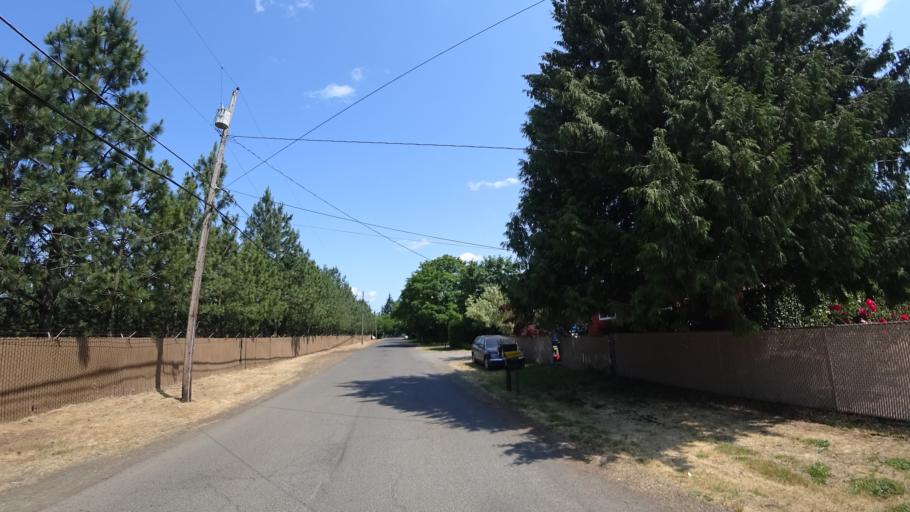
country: US
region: Oregon
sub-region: Multnomah County
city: Lents
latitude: 45.4499
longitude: -122.5826
